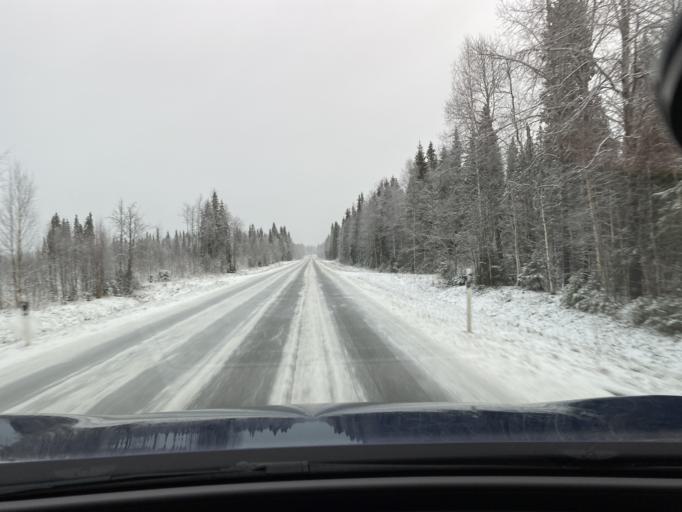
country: FI
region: Northern Ostrobothnia
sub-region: Oulu
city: Yli-Ii
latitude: 65.9446
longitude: 25.8968
